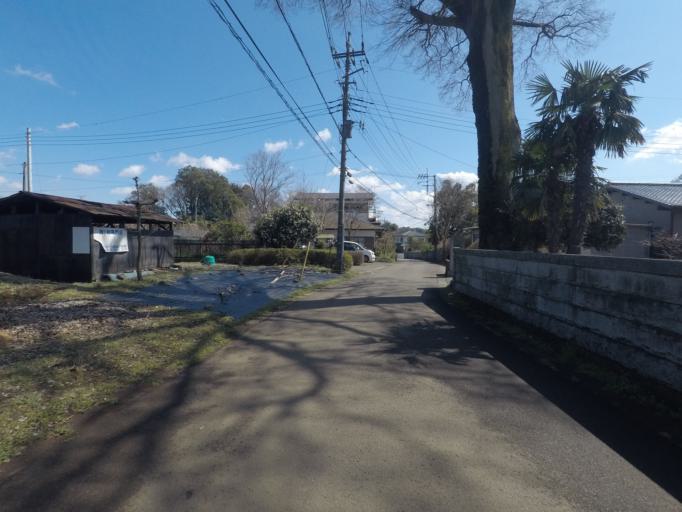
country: JP
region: Ibaraki
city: Ushiku
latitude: 36.0142
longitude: 140.0729
